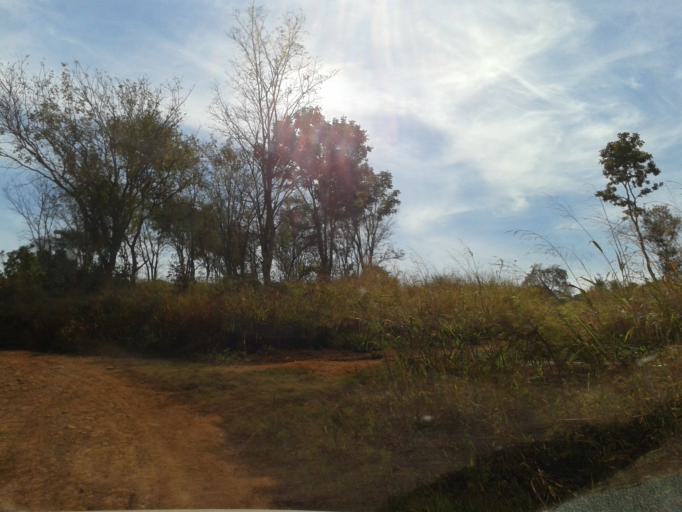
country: BR
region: Minas Gerais
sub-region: Ituiutaba
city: Ituiutaba
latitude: -18.9586
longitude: -49.4651
